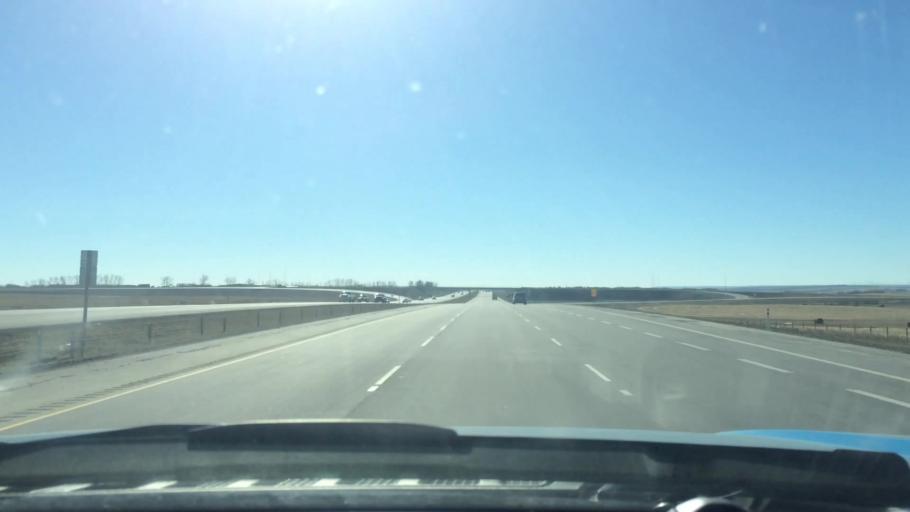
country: CA
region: Alberta
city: Crossfield
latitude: 51.3937
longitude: -114.0021
